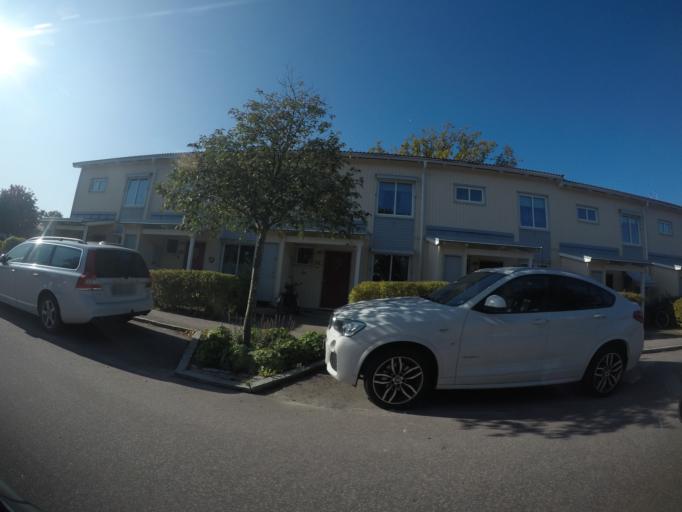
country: SE
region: Vaestmanland
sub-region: Vasteras
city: Vasteras
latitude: 59.6173
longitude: 16.5773
